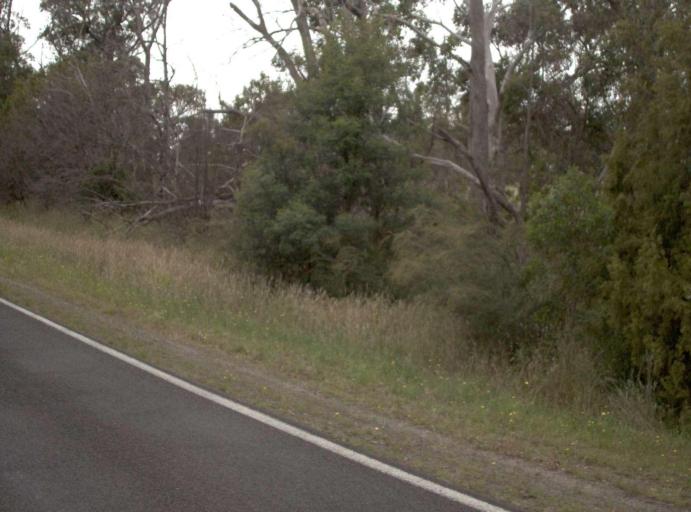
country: AU
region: Victoria
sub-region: Latrobe
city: Traralgon
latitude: -38.5407
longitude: 146.8409
